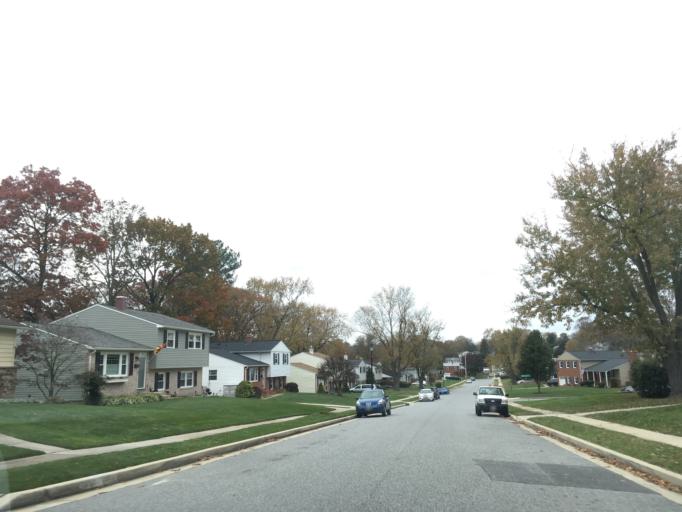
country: US
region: Maryland
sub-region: Baltimore County
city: Timonium
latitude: 39.4284
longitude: -76.6097
